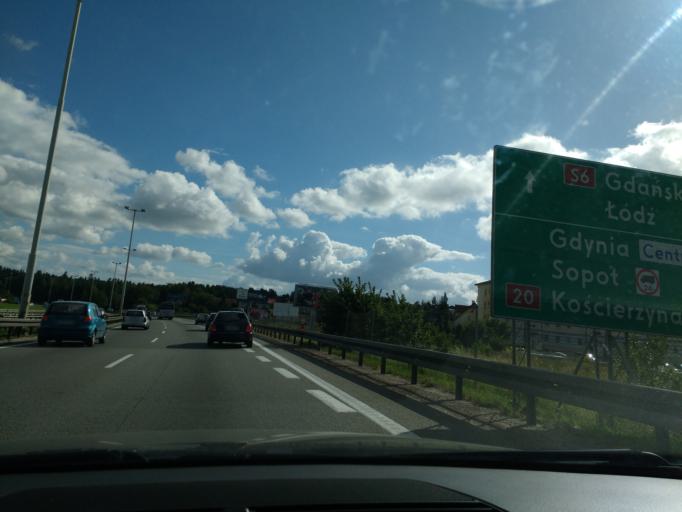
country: PL
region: Pomeranian Voivodeship
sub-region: Gdynia
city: Wielki Kack
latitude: 54.4742
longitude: 18.4720
